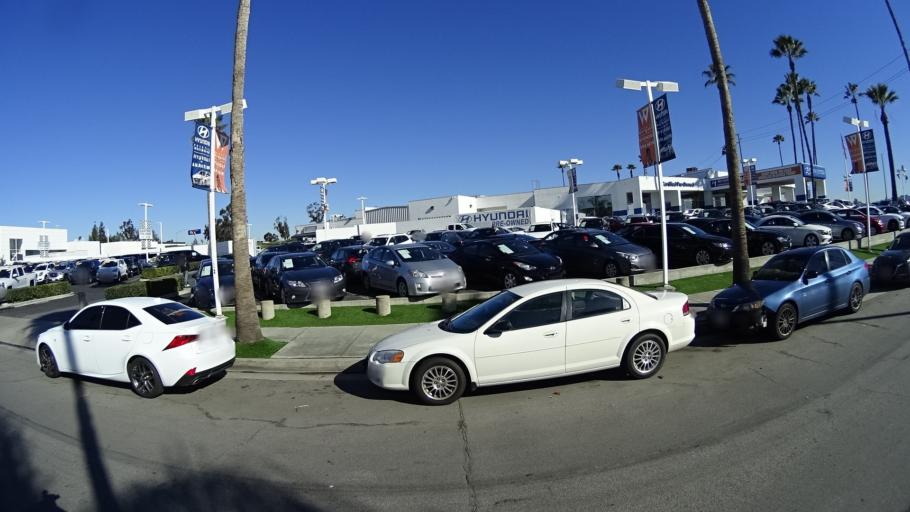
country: US
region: California
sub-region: Orange County
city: Orange
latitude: 33.8155
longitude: -117.8736
